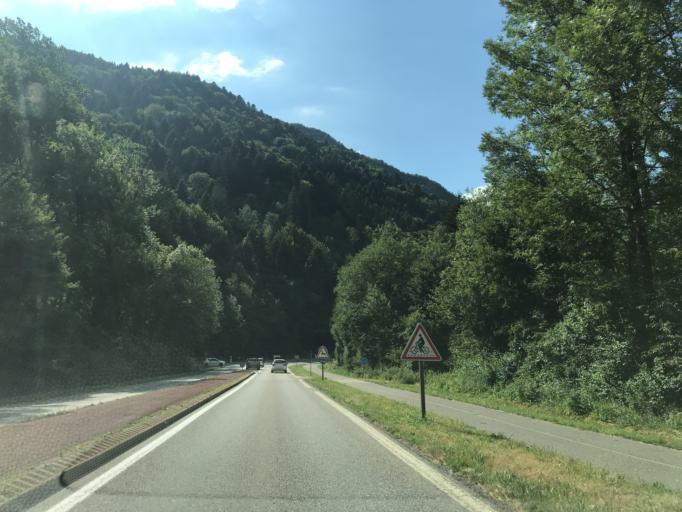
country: FR
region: Rhone-Alpes
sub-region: Departement de la Haute-Savoie
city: Dingy-Saint-Clair
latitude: 45.8987
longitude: 6.2160
